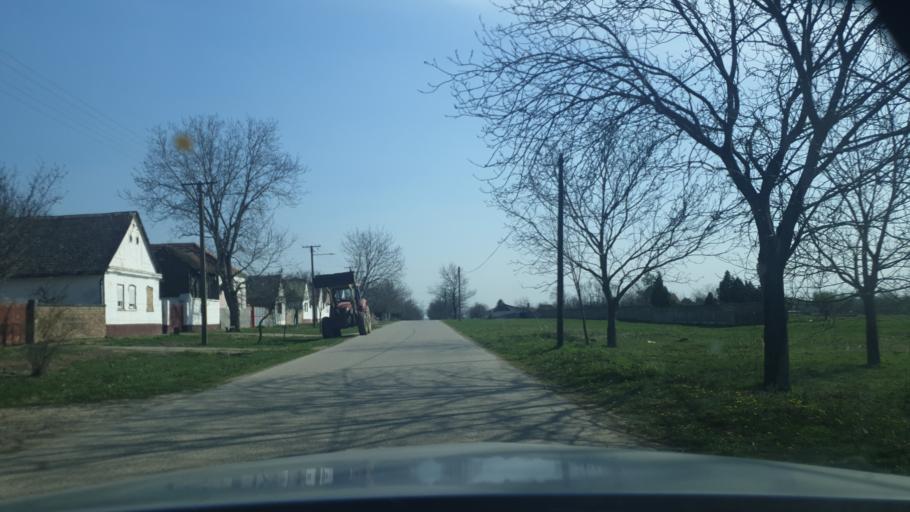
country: RS
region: Autonomna Pokrajina Vojvodina
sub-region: Sremski Okrug
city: Irig
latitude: 45.0654
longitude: 19.9233
